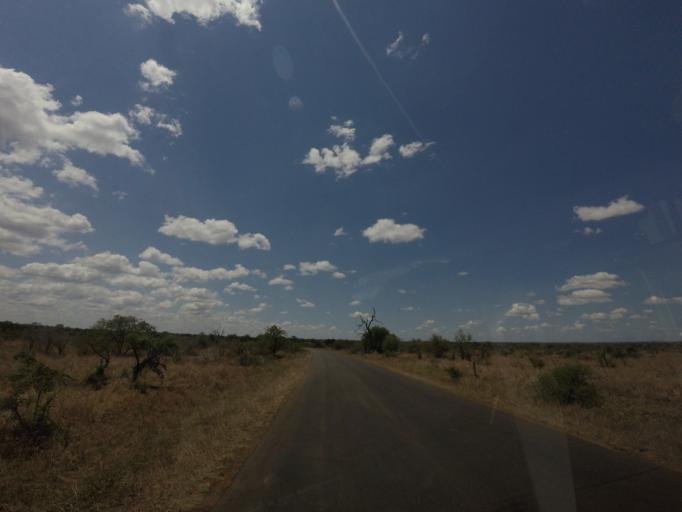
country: ZA
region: Limpopo
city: Thulamahashi
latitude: -24.4032
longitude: 31.7870
